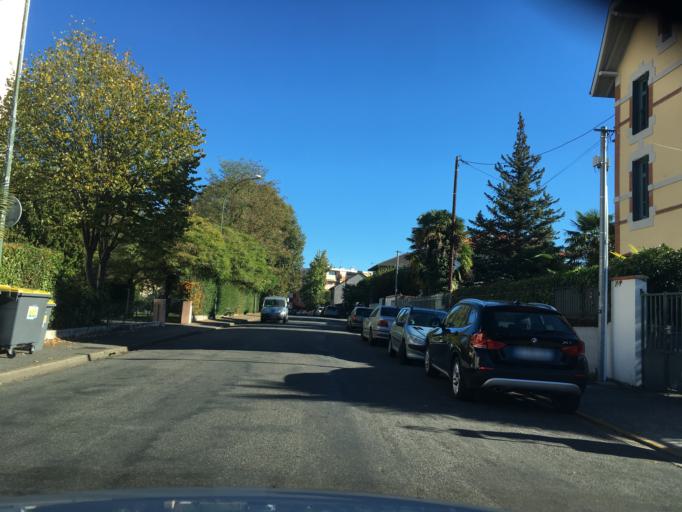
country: FR
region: Aquitaine
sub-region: Departement des Pyrenees-Atlantiques
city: Pau
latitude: 43.3046
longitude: -0.3551
